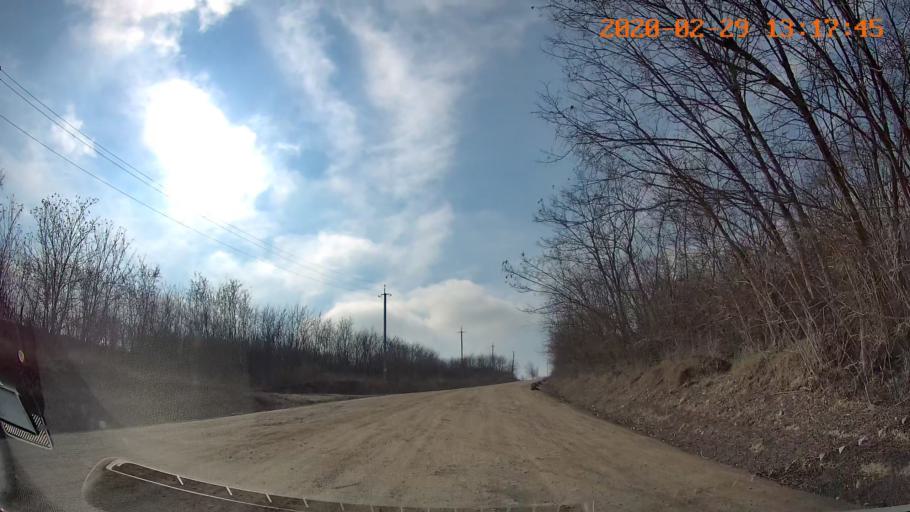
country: MD
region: Telenesti
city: Camenca
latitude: 47.9954
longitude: 28.6614
